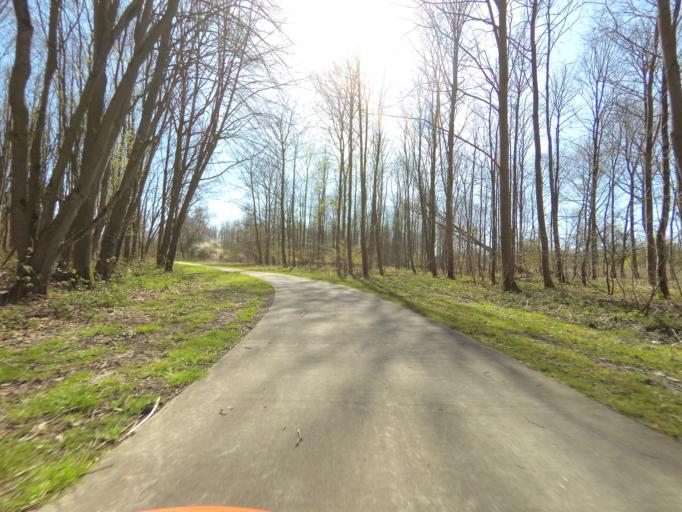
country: NL
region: Flevoland
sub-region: Gemeente Zeewolde
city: Zeewolde
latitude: 52.3134
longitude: 5.4894
